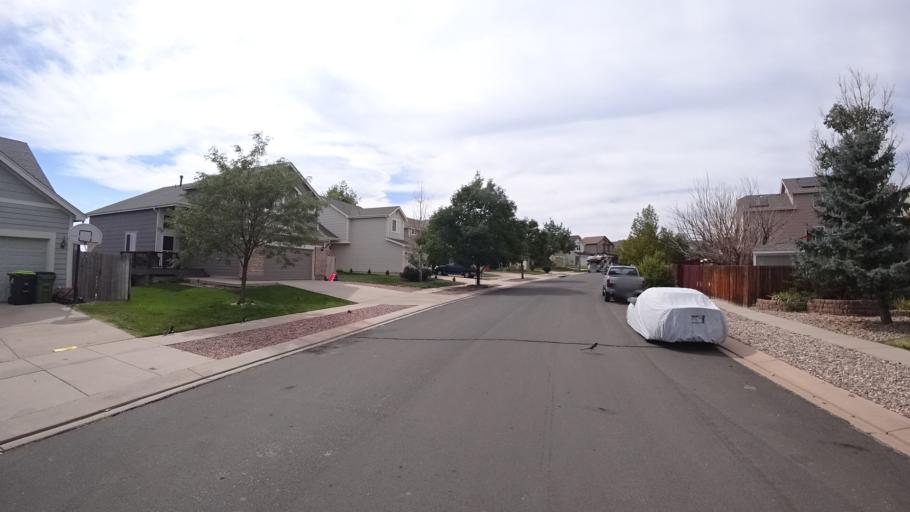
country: US
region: Colorado
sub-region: El Paso County
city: Cimarron Hills
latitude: 38.8980
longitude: -104.7170
